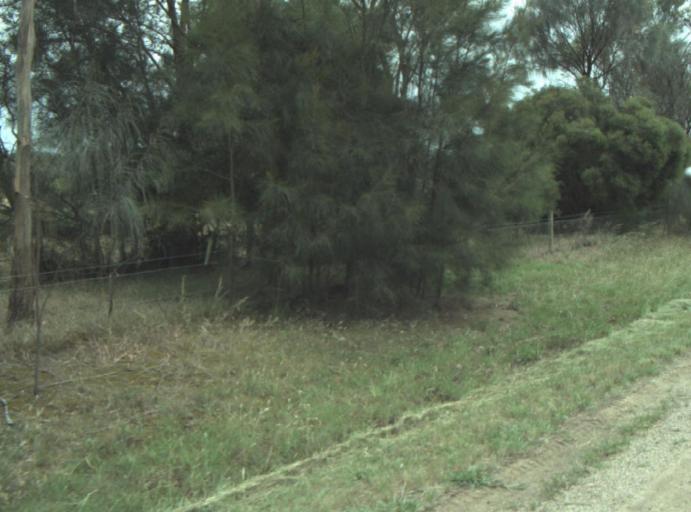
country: AU
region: Victoria
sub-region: Greater Geelong
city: Lara
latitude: -38.0059
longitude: 144.4182
